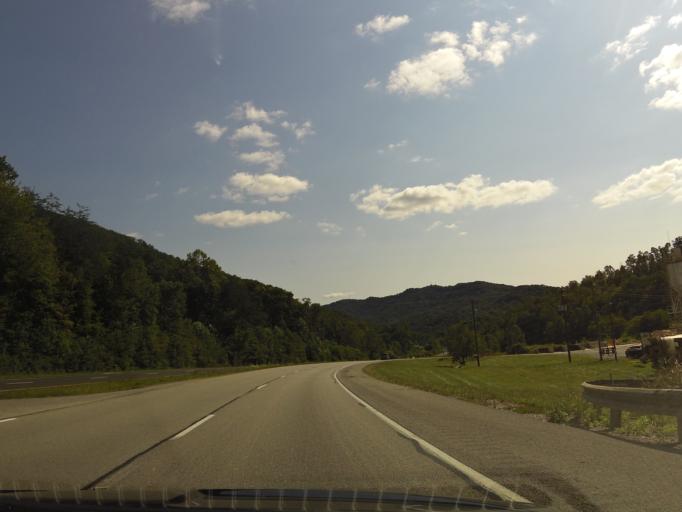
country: US
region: Kentucky
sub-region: Bell County
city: Middlesboro
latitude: 36.6771
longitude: -83.6846
